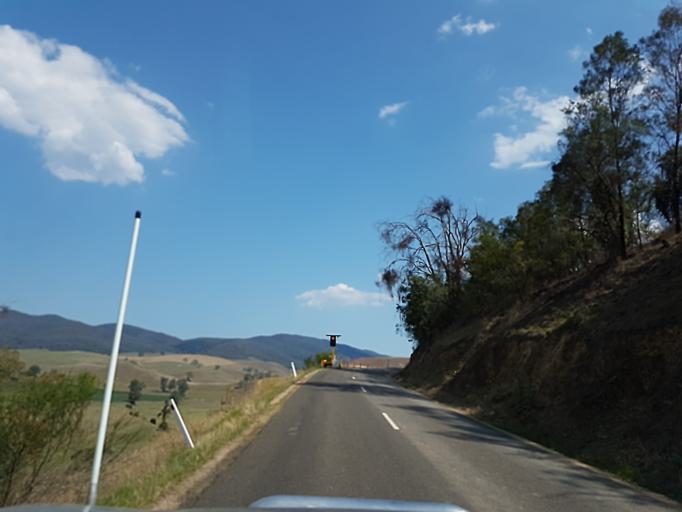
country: AU
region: Victoria
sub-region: East Gippsland
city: Lakes Entrance
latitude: -37.4989
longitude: 148.1917
